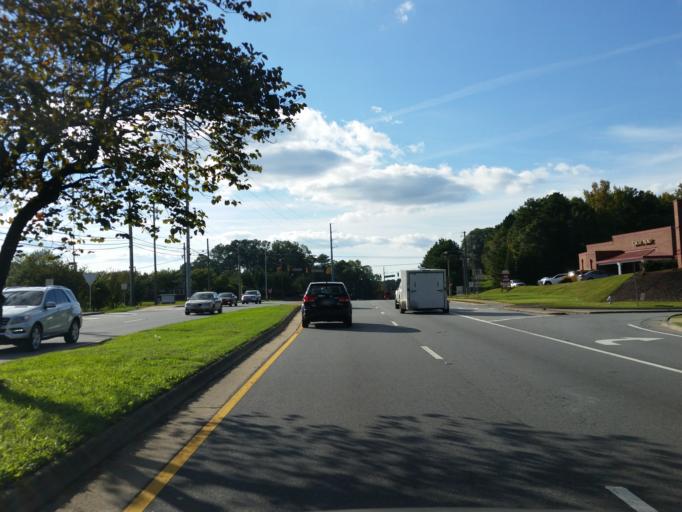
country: US
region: Georgia
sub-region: Cobb County
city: Kennesaw
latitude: 33.9466
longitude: -84.6290
